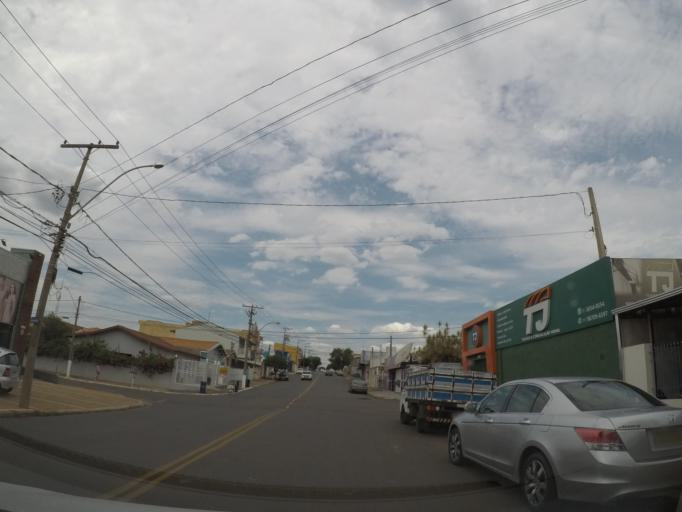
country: BR
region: Sao Paulo
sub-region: Sumare
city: Sumare
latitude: -22.8284
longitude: -47.2746
